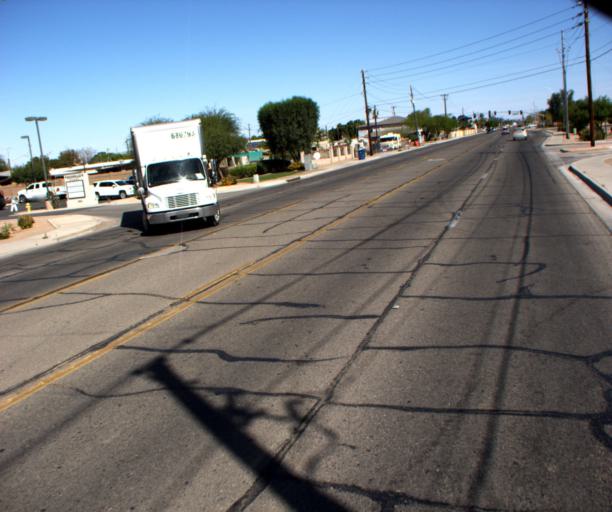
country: US
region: Arizona
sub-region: Yuma County
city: Yuma
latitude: 32.6785
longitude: -114.6502
